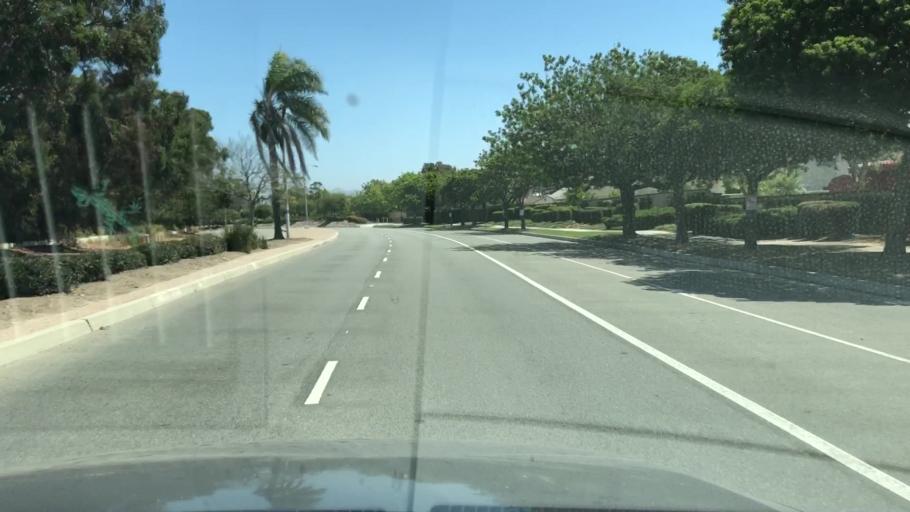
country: US
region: California
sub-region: Ventura County
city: El Rio
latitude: 34.2367
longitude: -119.1920
